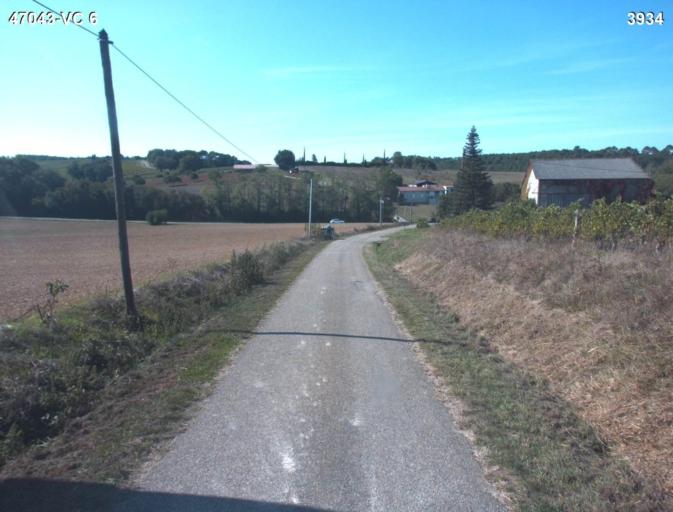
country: FR
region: Aquitaine
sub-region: Departement du Lot-et-Garonne
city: Buzet-sur-Baise
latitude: 44.2303
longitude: 0.2779
